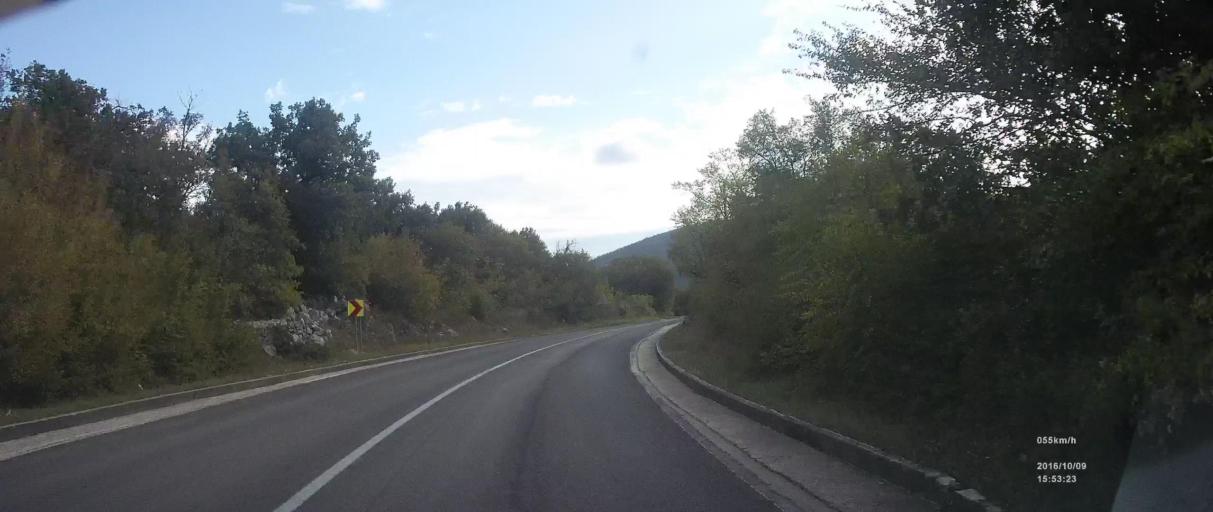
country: HR
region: Splitsko-Dalmatinska
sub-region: Grad Trogir
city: Trogir
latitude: 43.6058
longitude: 16.2251
